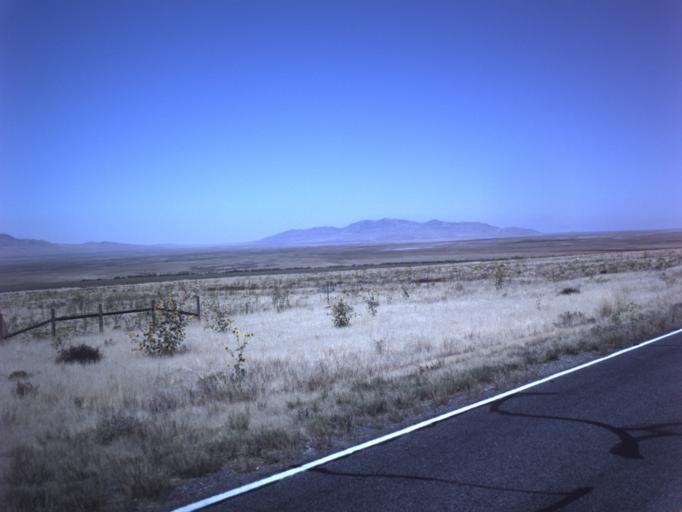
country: US
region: Utah
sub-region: Tooele County
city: Grantsville
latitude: 40.5899
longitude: -112.7209
